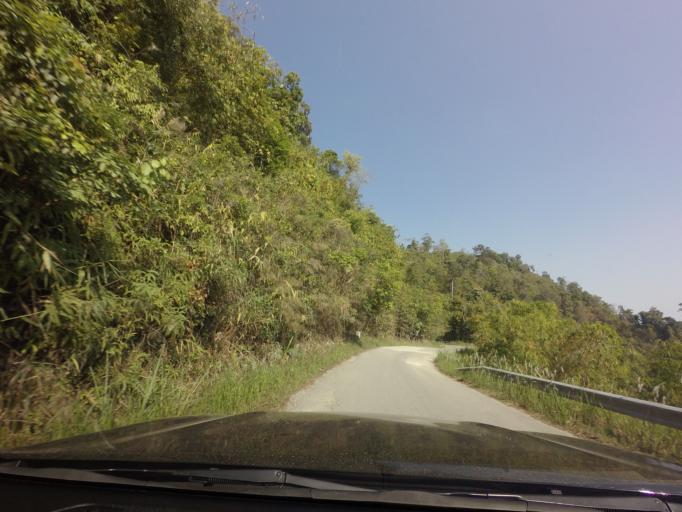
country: TH
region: Kanchanaburi
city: Thong Pha Phum
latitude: 14.6922
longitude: 98.4573
